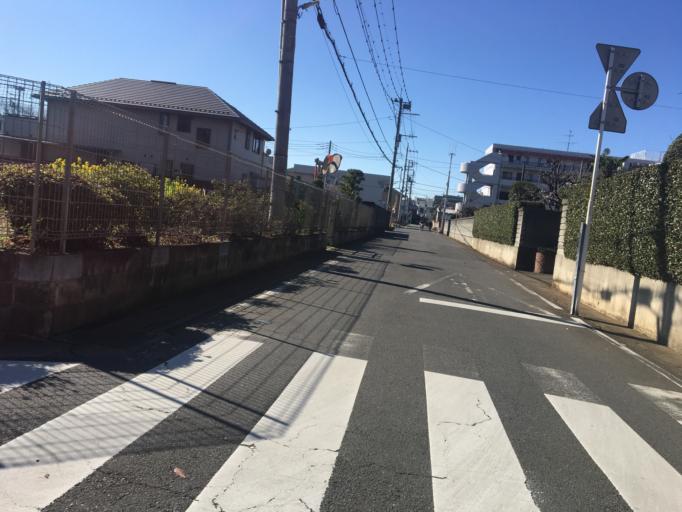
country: JP
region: Saitama
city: Shiki
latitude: 35.8181
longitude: 139.5739
